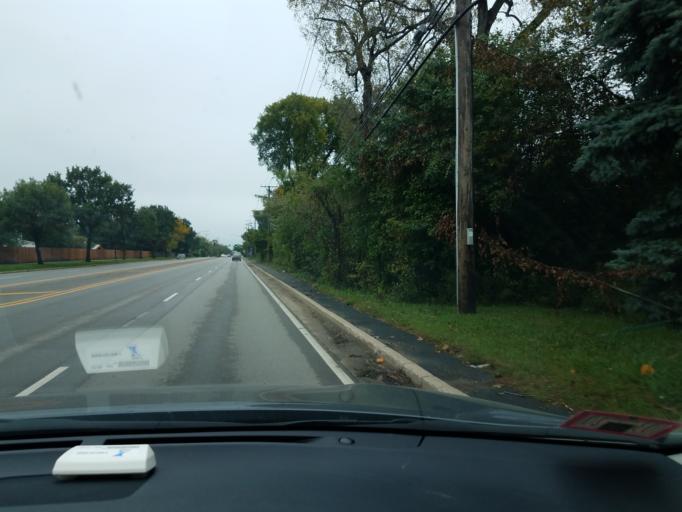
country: US
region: Illinois
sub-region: Cook County
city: Buffalo Grove
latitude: 42.1828
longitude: -87.9522
